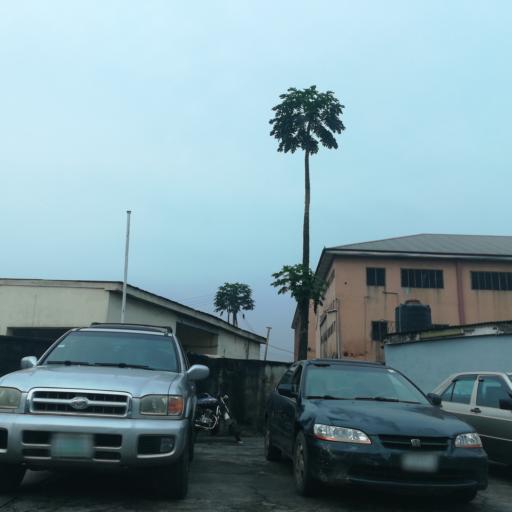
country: NG
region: Rivers
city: Port Harcourt
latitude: 4.7661
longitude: 7.0123
